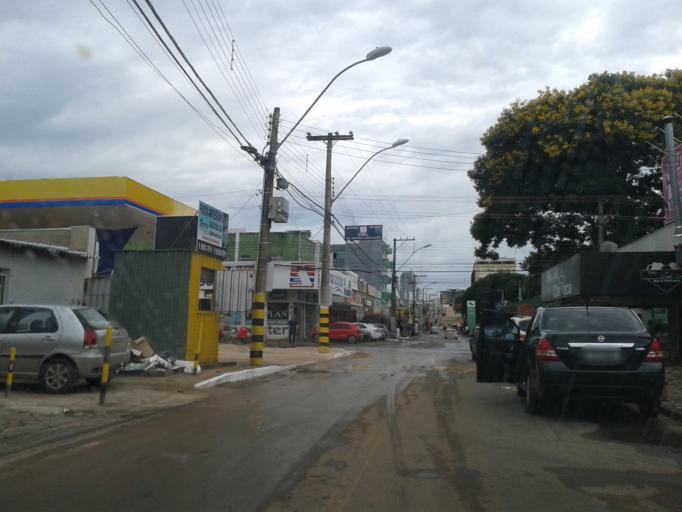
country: BR
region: Federal District
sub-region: Brasilia
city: Brasilia
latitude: -15.8252
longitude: -48.0576
